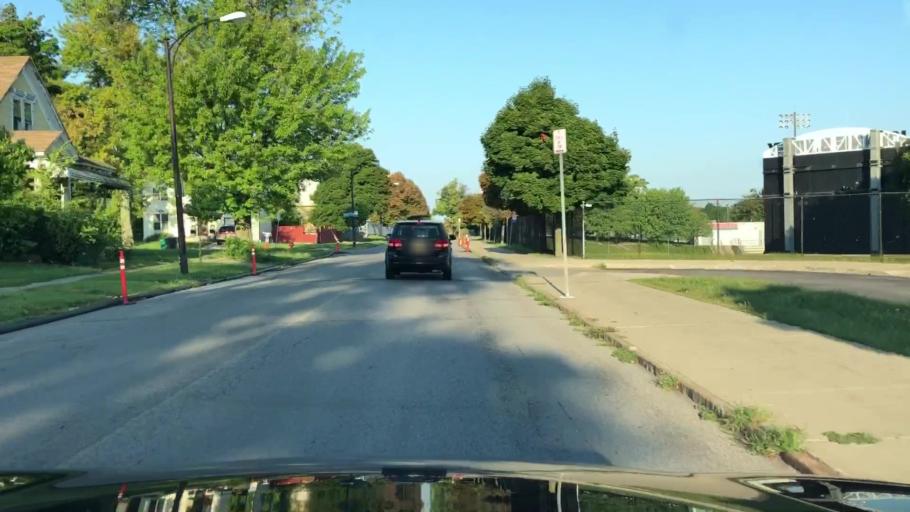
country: US
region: New York
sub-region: Erie County
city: Buffalo
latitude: 42.9039
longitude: -78.8555
